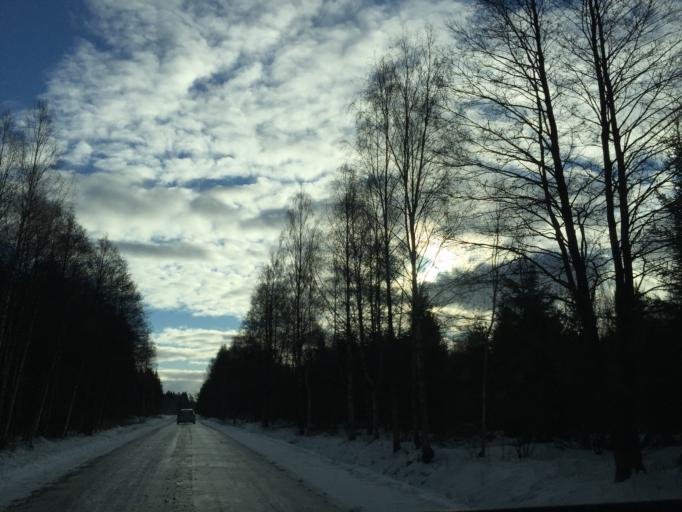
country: LV
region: Ogre
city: Jumprava
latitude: 56.5531
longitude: 24.8574
